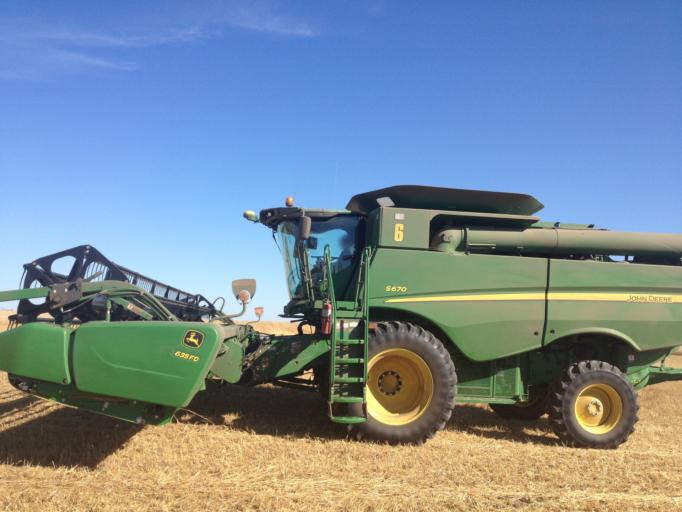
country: US
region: North Dakota
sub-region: Mountrail County
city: New Town
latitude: 47.8043
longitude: -101.9928
